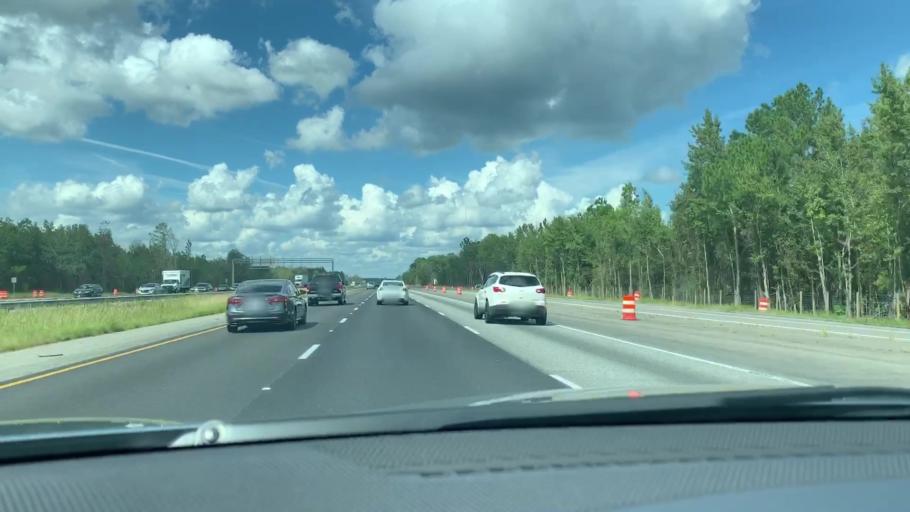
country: US
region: Georgia
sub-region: Camden County
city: Kingsland
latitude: 30.8499
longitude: -81.6736
